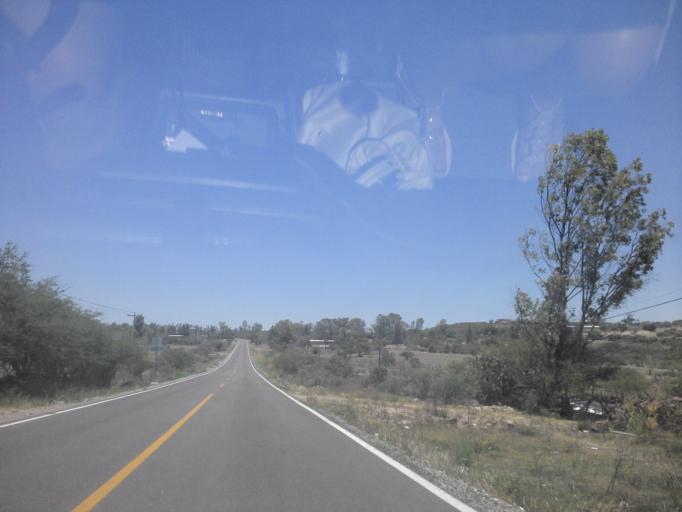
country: MX
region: Guanajuato
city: Ciudad Manuel Doblado
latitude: 20.8240
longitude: -102.0005
